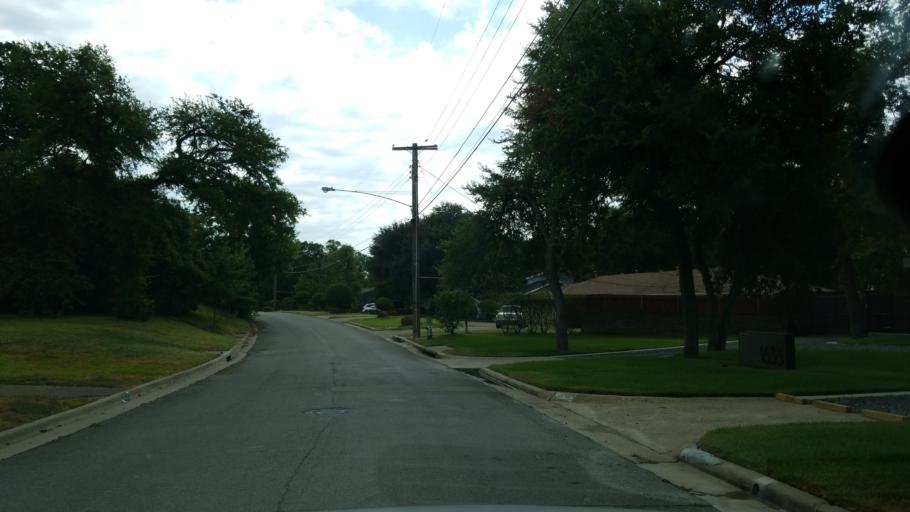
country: US
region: Texas
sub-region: Dallas County
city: Duncanville
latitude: 32.6699
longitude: -96.8487
